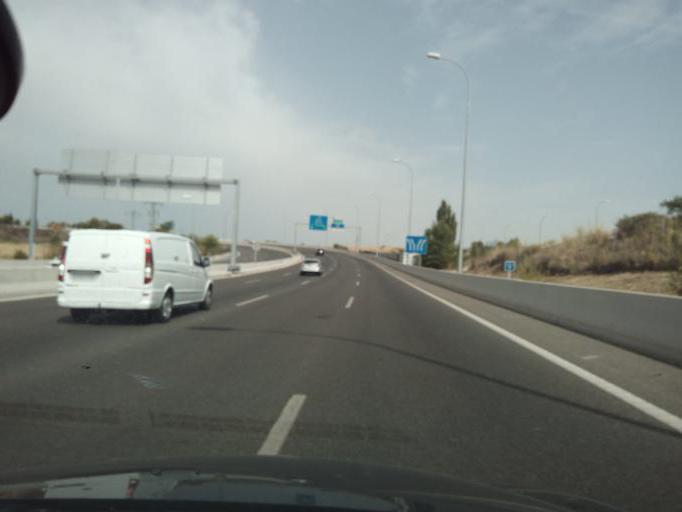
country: ES
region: Madrid
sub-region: Provincia de Madrid
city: Hortaleza
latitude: 40.4790
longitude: -3.6346
